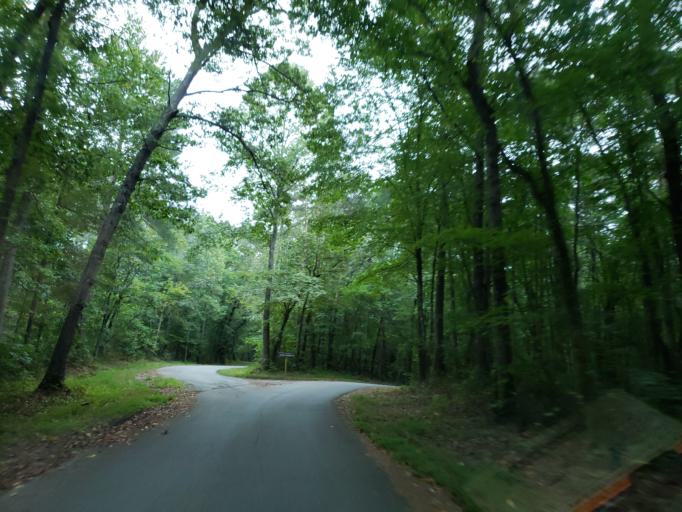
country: US
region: Georgia
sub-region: Cherokee County
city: Ball Ground
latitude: 34.3520
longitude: -84.4834
